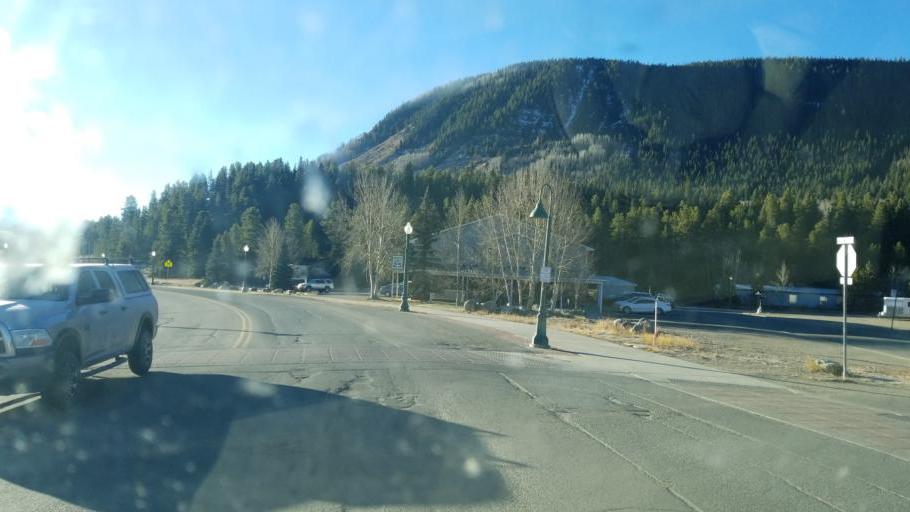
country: US
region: Colorado
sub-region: Gunnison County
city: Crested Butte
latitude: 38.8669
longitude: -106.9761
